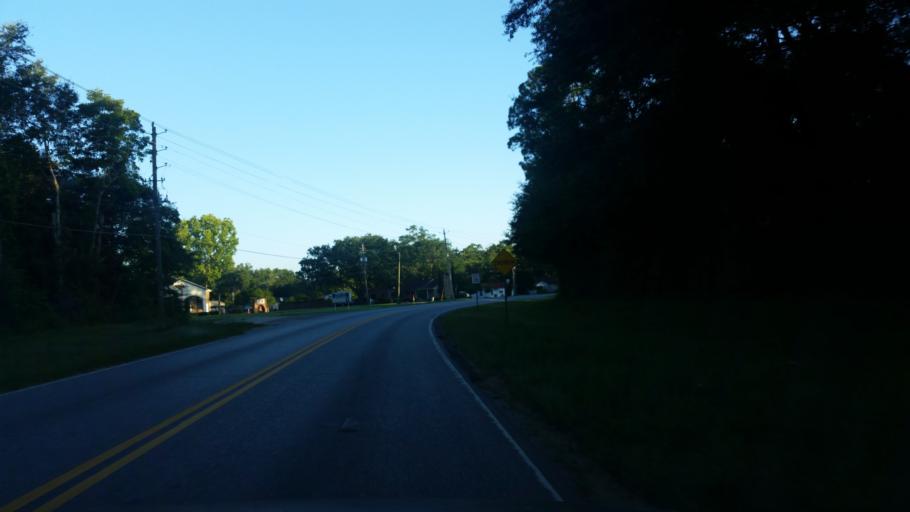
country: US
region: Florida
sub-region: Escambia County
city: Cantonment
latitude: 30.6027
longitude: -87.3308
